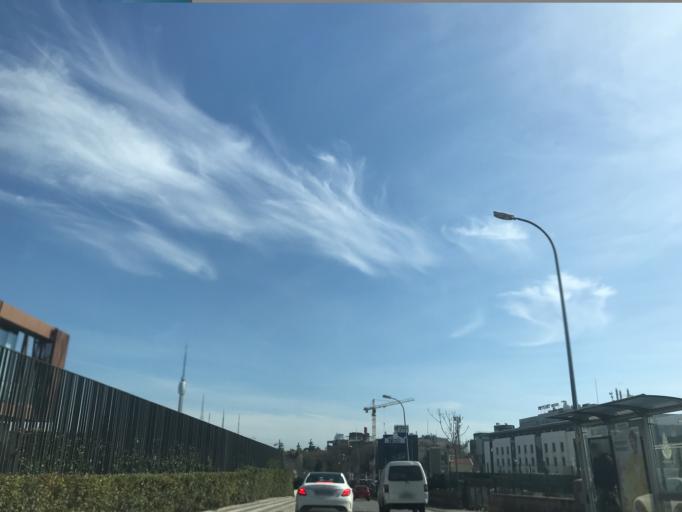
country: TR
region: Istanbul
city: UEskuedar
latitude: 41.0264
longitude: 29.0407
